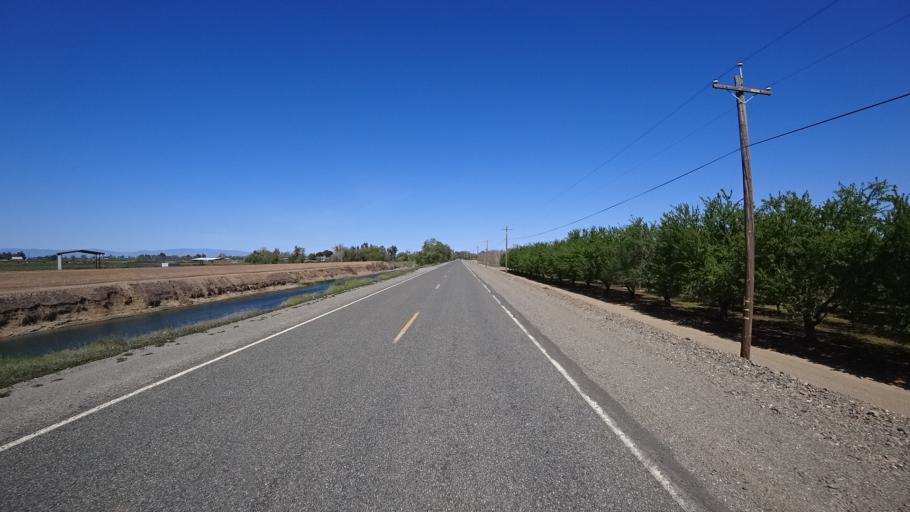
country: US
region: California
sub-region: Glenn County
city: Hamilton City
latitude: 39.7787
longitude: -122.0412
